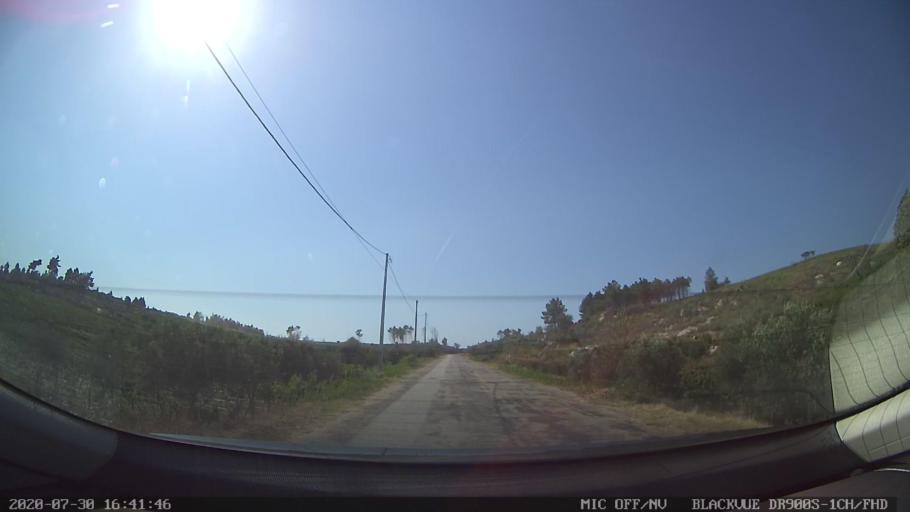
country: PT
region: Vila Real
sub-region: Sabrosa
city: Sabrosa
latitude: 41.2965
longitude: -7.4818
